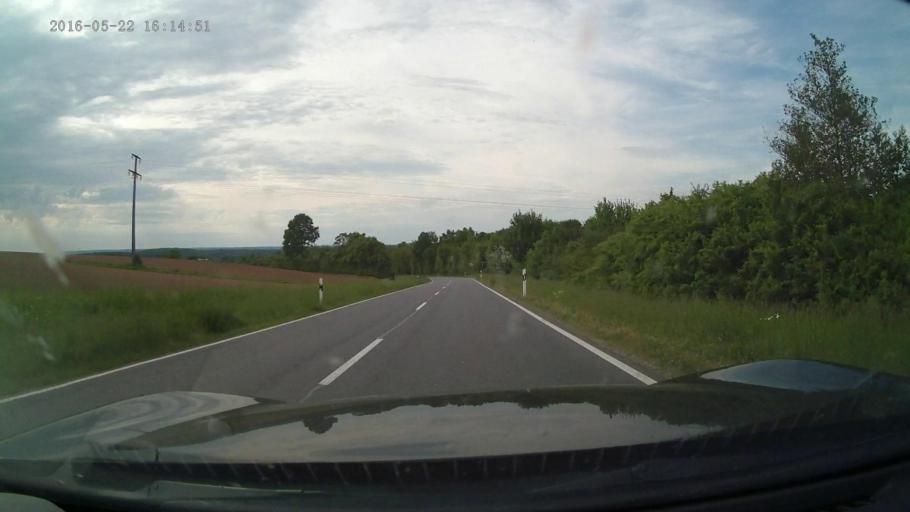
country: DE
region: Baden-Wuerttemberg
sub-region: Karlsruhe Region
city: Osterburken
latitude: 49.4245
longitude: 9.4402
